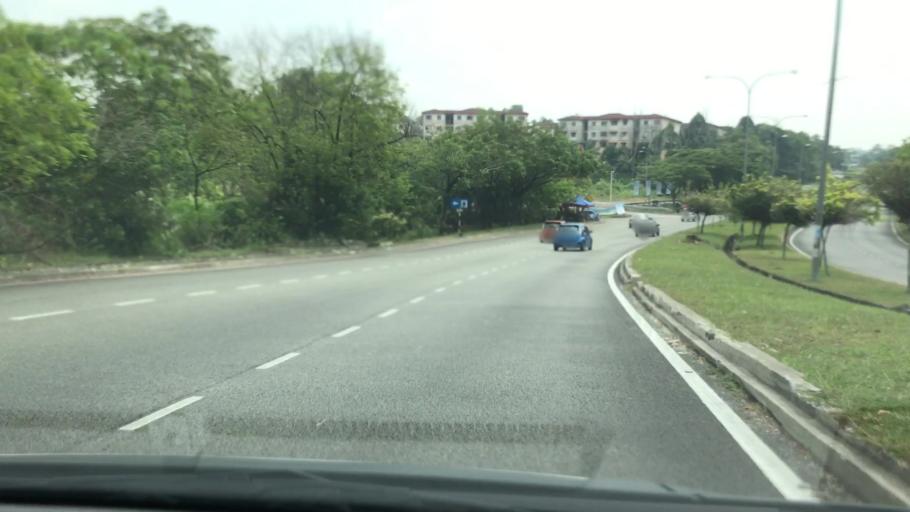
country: MY
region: Putrajaya
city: Putrajaya
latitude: 2.9928
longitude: 101.6631
